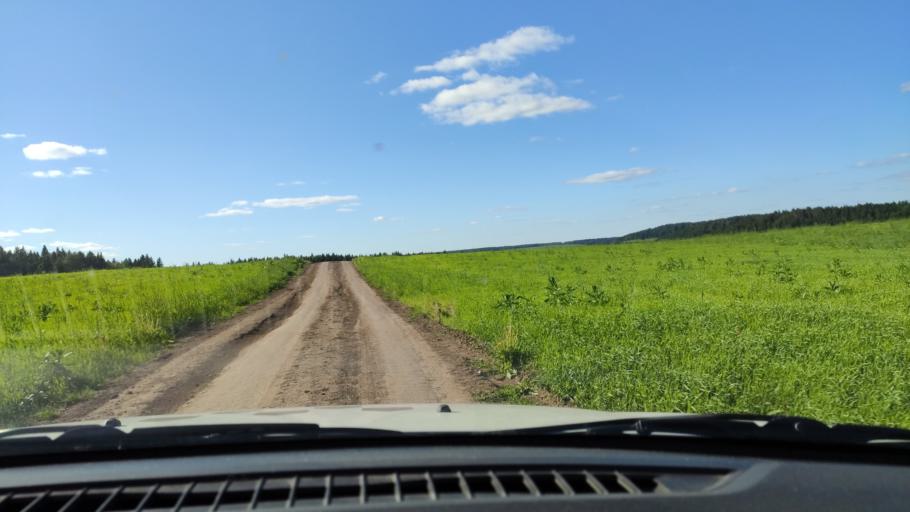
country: RU
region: Perm
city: Orda
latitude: 57.2976
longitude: 56.5931
